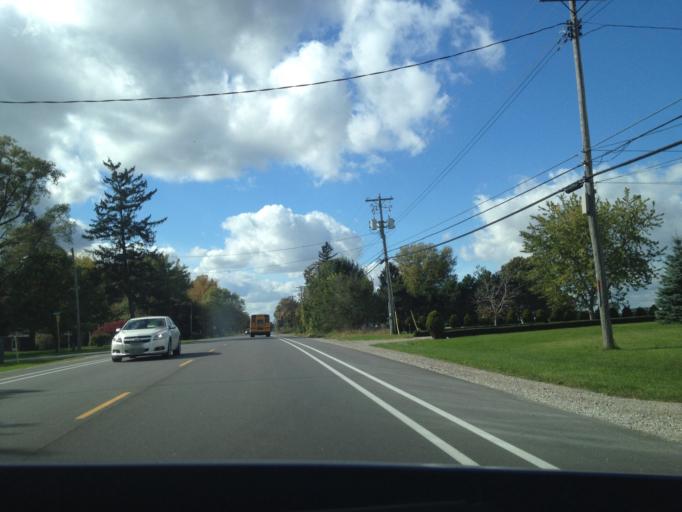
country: CA
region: Ontario
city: Amherstburg
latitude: 42.0358
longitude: -82.7043
